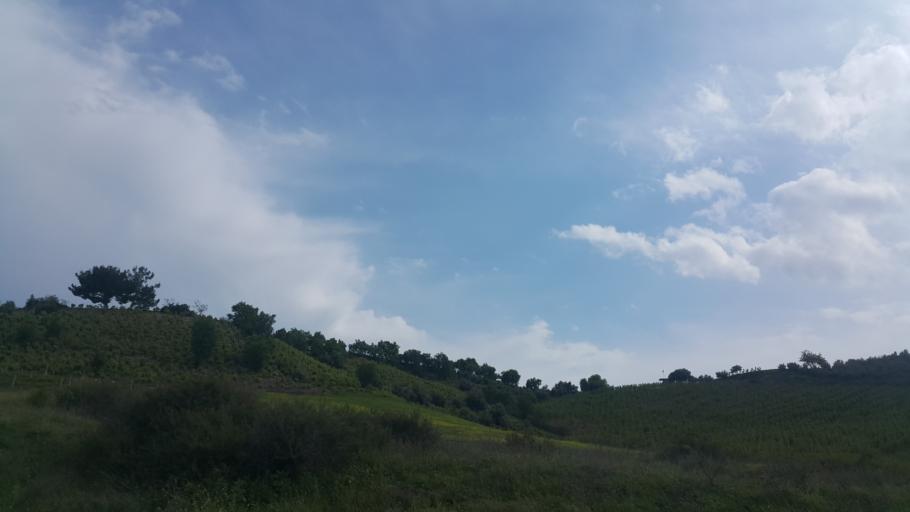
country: TR
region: Mersin
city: Tarsus
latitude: 36.9552
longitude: 34.7579
